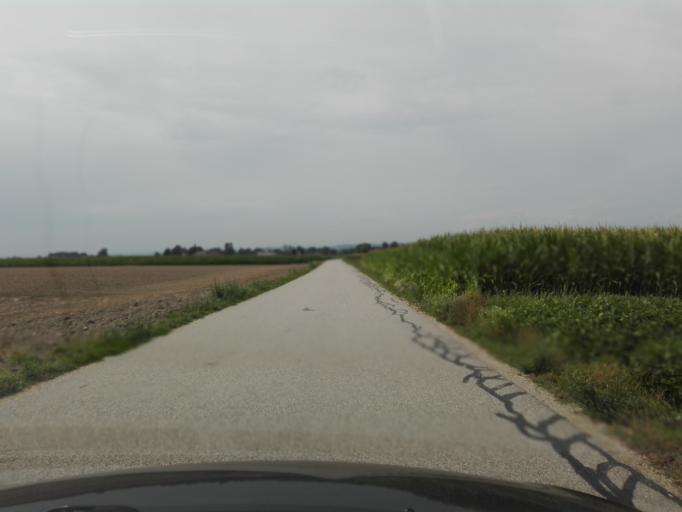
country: AT
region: Lower Austria
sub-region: Politischer Bezirk Amstetten
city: Strengberg
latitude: 48.1798
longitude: 14.7000
